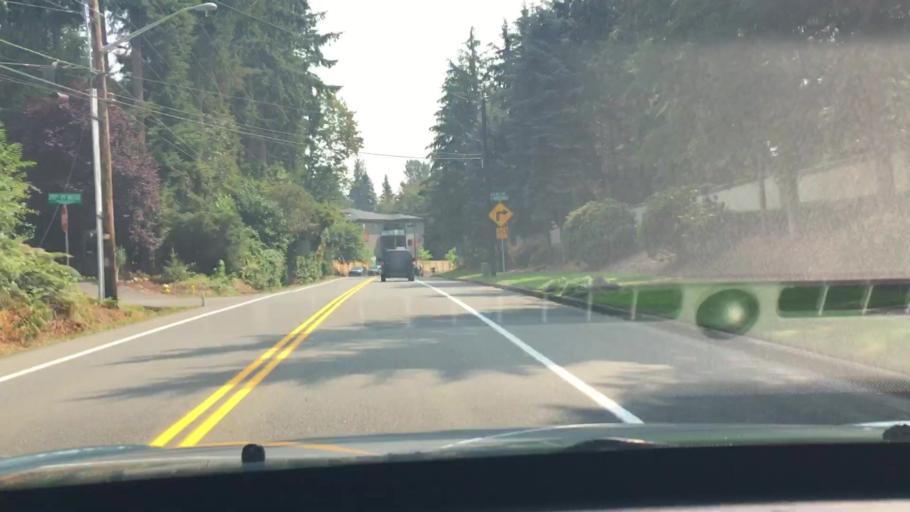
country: US
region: Washington
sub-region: King County
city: City of Sammamish
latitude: 47.6064
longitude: -122.0581
